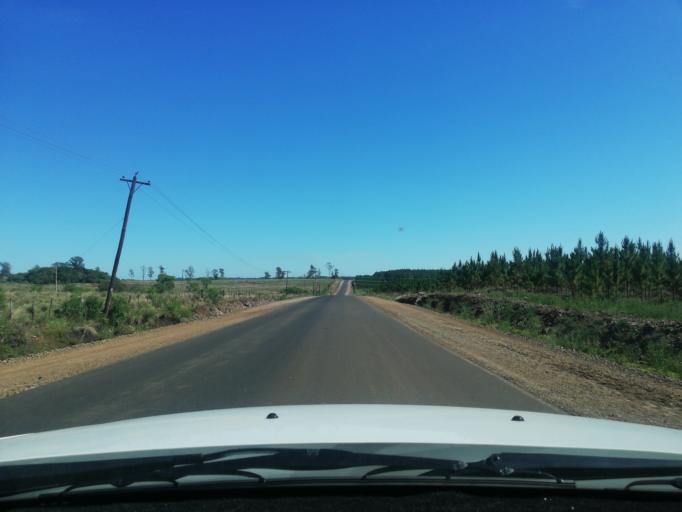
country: AR
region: Misiones
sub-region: Departamento de Candelaria
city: Candelaria
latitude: -27.5083
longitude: -55.7364
